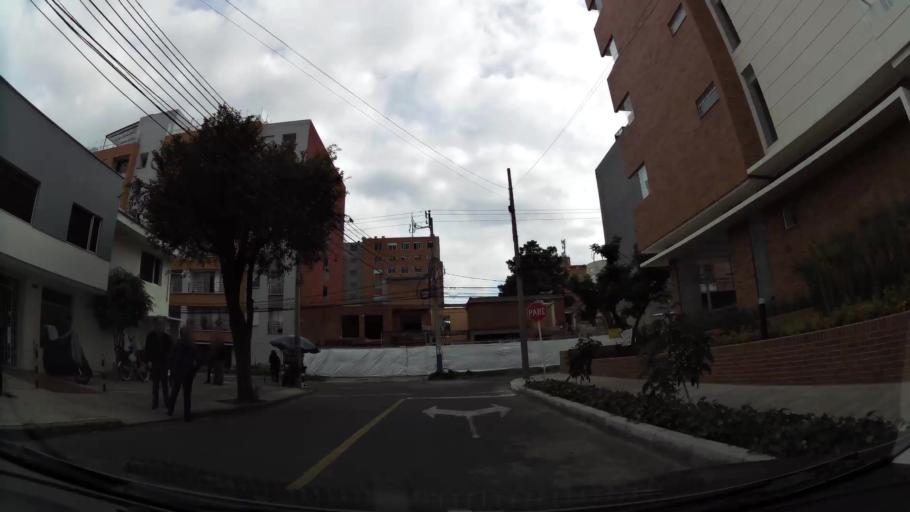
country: CO
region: Bogota D.C.
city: Barrio San Luis
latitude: 4.7010
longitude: -74.0303
